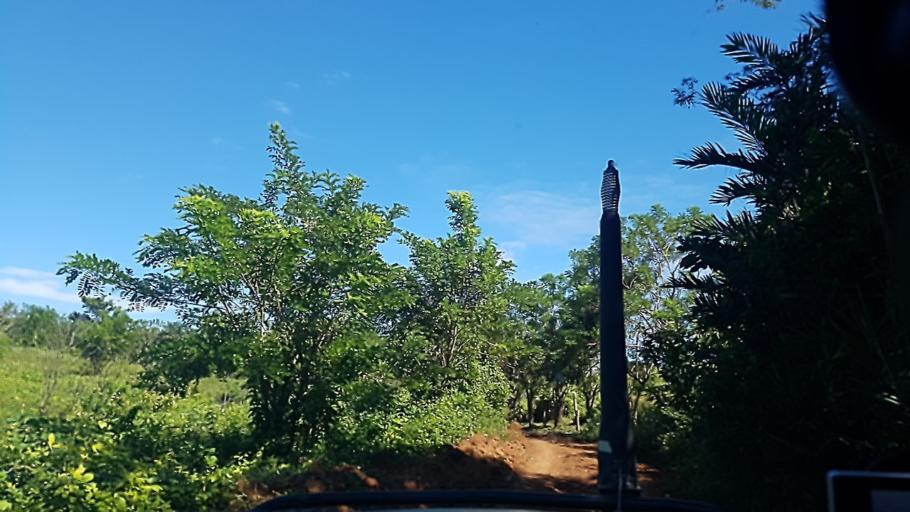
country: NI
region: Granada
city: Nandaime
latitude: 11.5783
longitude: -86.0976
